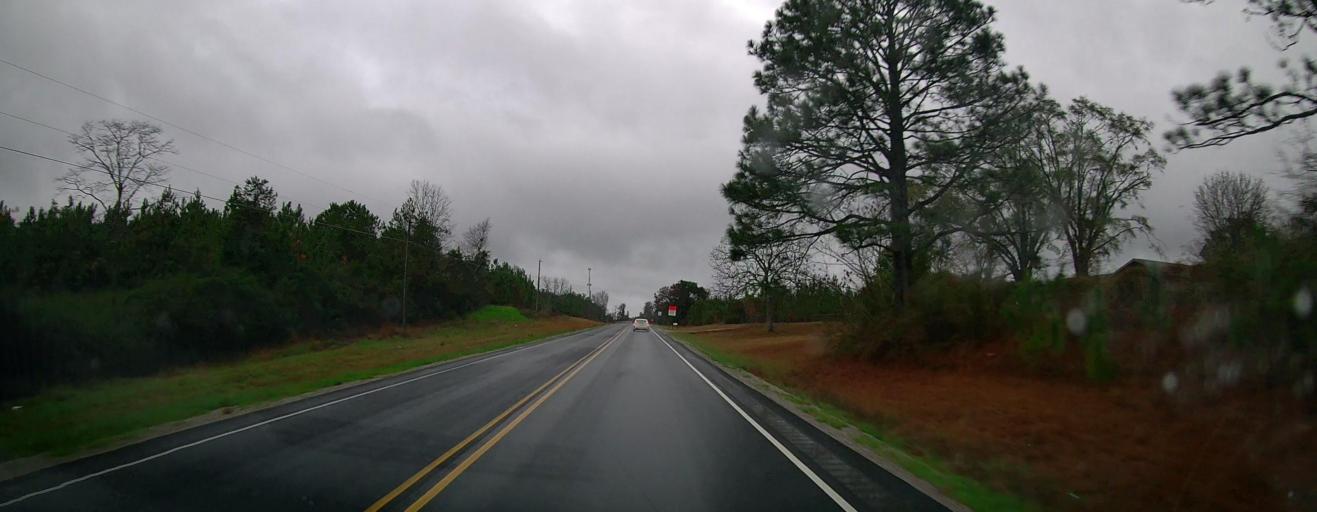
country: US
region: Alabama
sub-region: Chilton County
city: Clanton
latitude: 32.6347
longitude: -86.7487
